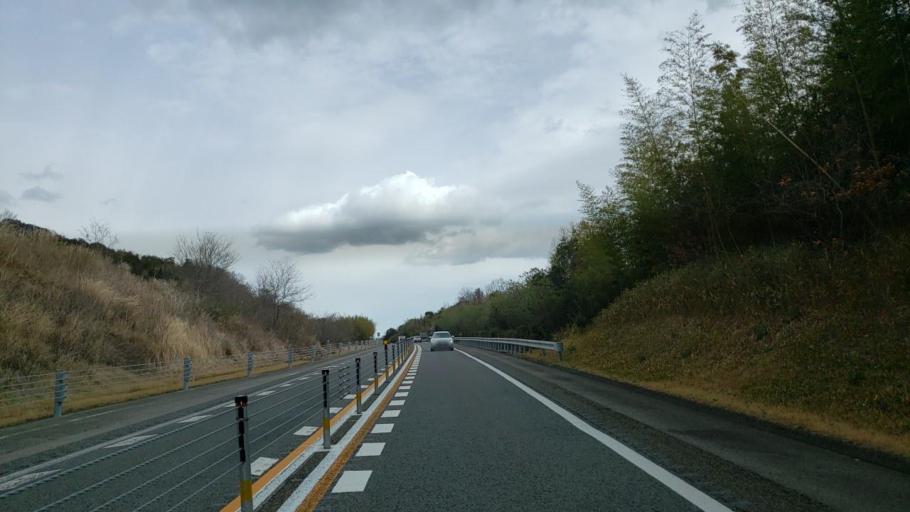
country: JP
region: Tokushima
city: Kamojimacho-jogejima
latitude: 34.1213
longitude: 134.3754
